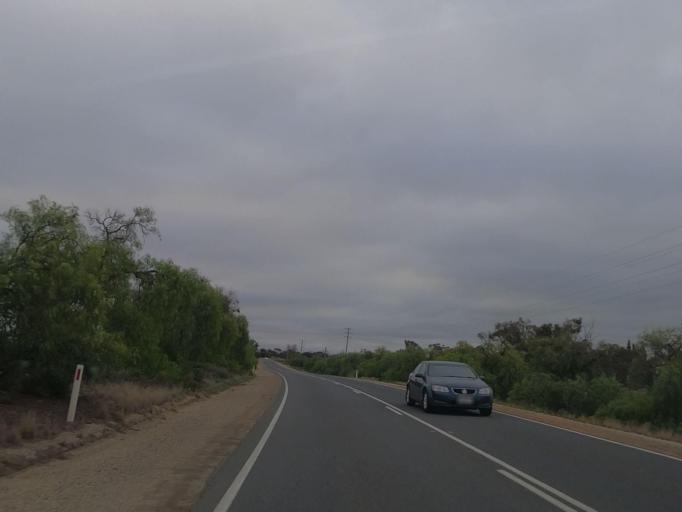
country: AU
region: Victoria
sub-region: Swan Hill
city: Swan Hill
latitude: -35.4456
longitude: 143.6197
